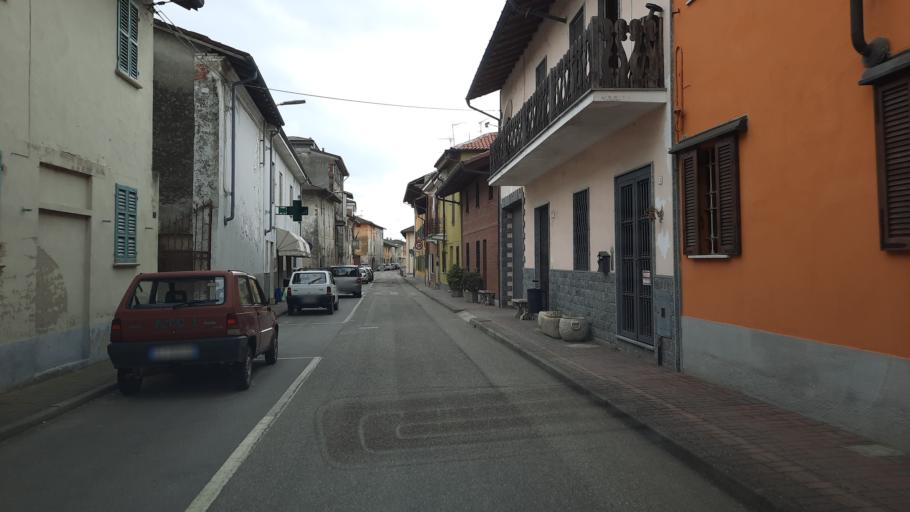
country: IT
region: Lombardy
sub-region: Provincia di Pavia
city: Castelnovetto
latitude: 45.2548
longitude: 8.6130
